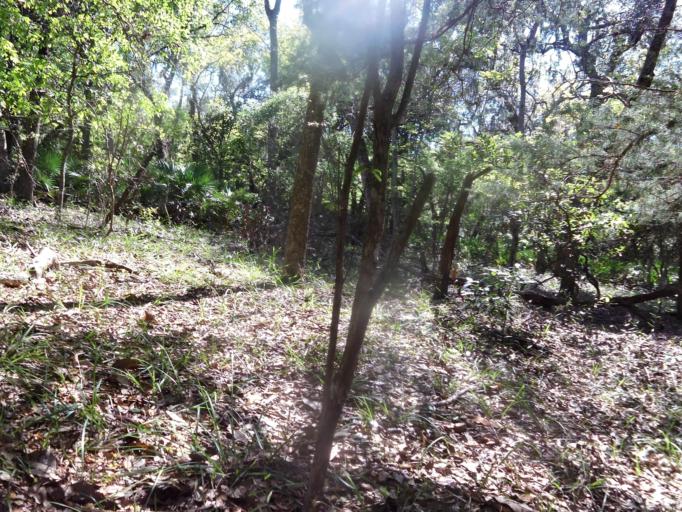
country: US
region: Florida
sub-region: Saint Johns County
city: Villano Beach
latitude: 29.9962
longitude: -81.3268
